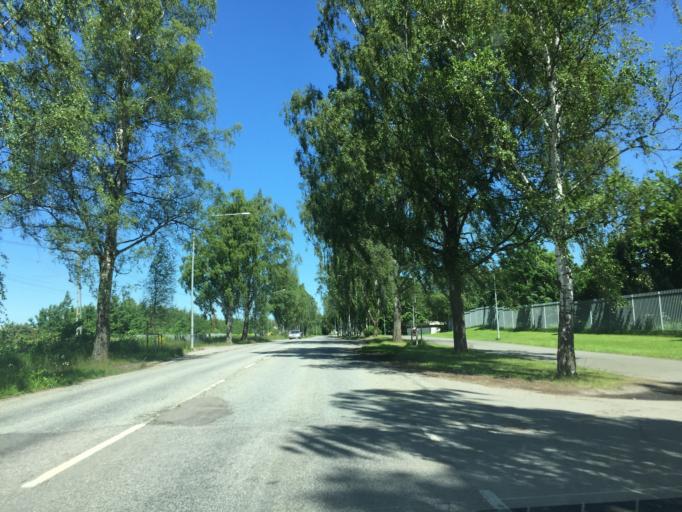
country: SE
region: OErebro
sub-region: Orebro Kommun
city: Orebro
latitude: 59.2593
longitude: 15.1900
